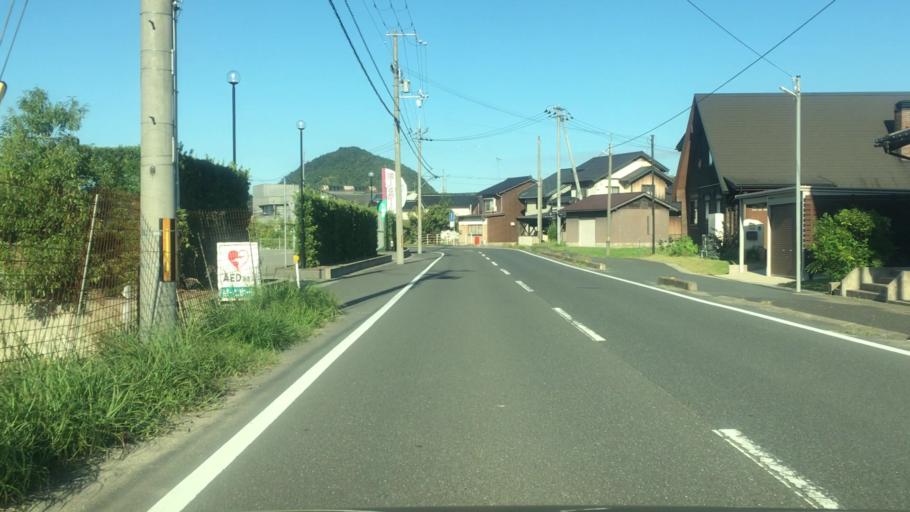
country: JP
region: Hyogo
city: Toyooka
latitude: 35.6022
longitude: 134.8930
